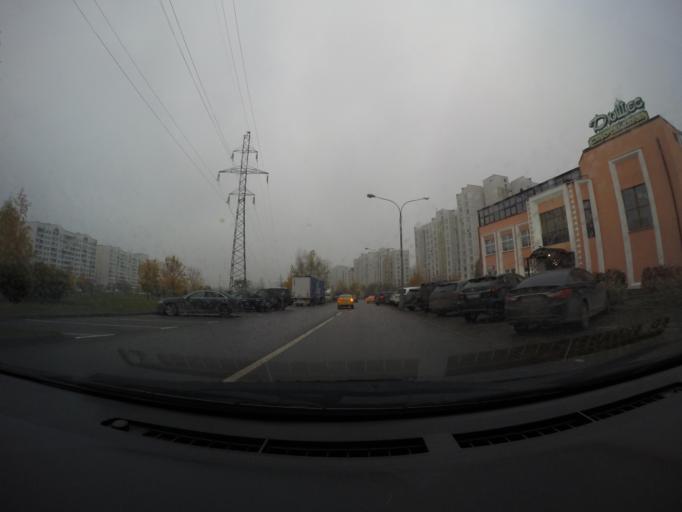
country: RU
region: Moskovskaya
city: Kommunarka
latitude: 55.5481
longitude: 37.5230
